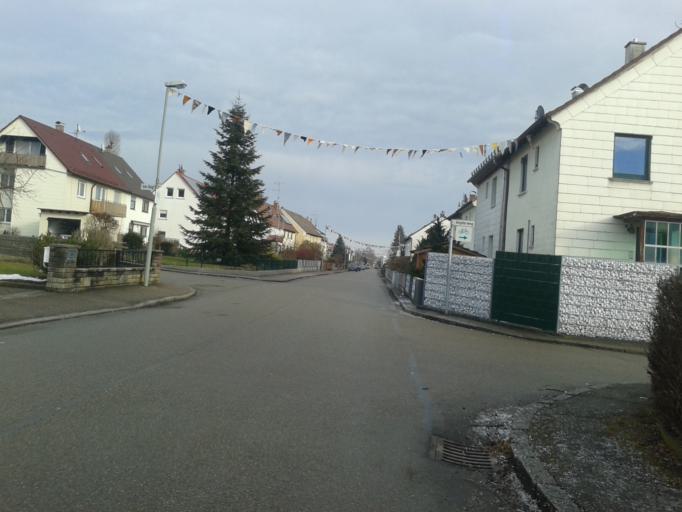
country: DE
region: Baden-Wuerttemberg
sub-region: Tuebingen Region
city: Erbach
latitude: 48.3535
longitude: 9.9050
